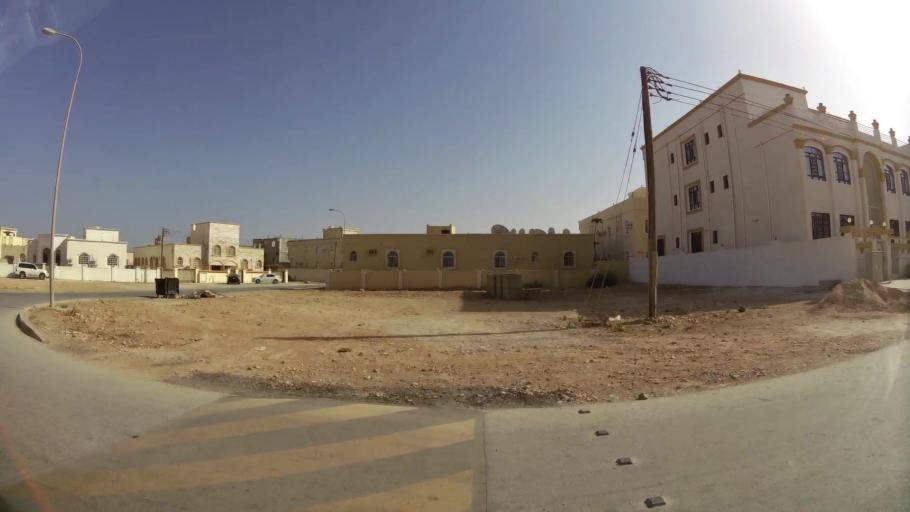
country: OM
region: Zufar
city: Salalah
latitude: 17.0146
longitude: 54.0116
